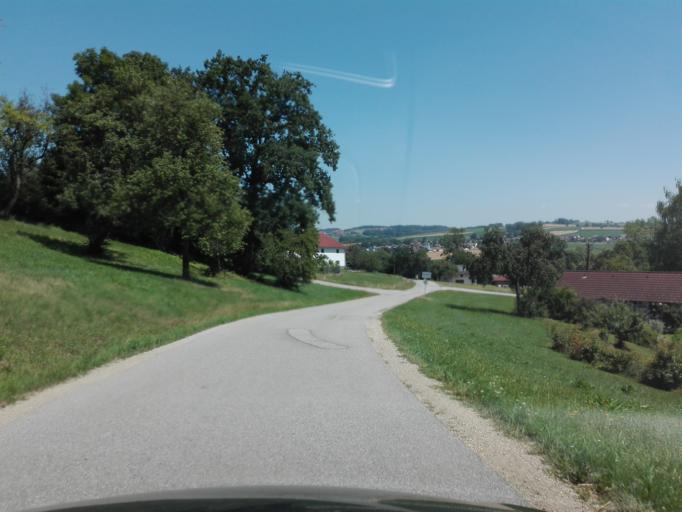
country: AT
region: Upper Austria
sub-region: Politischer Bezirk Urfahr-Umgebung
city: Engerwitzdorf
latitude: 48.2932
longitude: 14.4701
